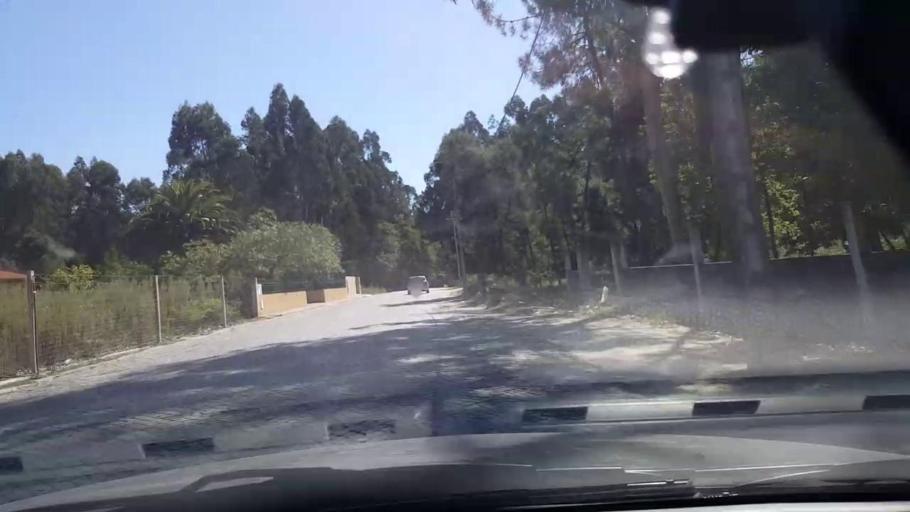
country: PT
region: Porto
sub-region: Vila do Conde
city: Arvore
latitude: 41.3288
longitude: -8.7284
